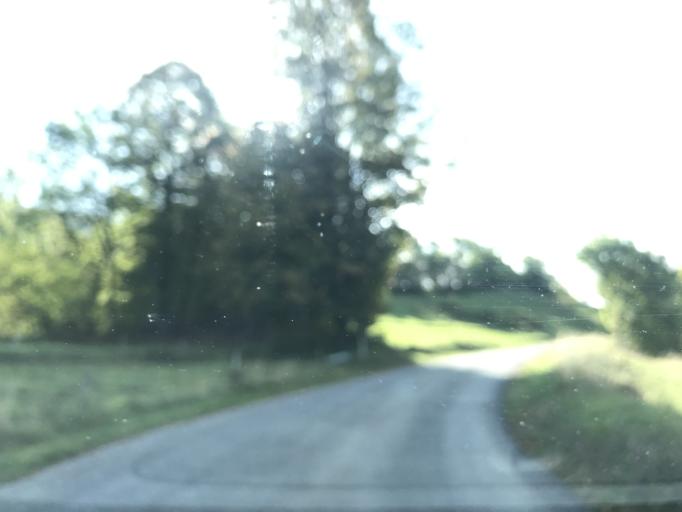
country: FR
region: Rhone-Alpes
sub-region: Departement de la Savoie
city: Novalaise
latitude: 45.6367
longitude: 5.7995
